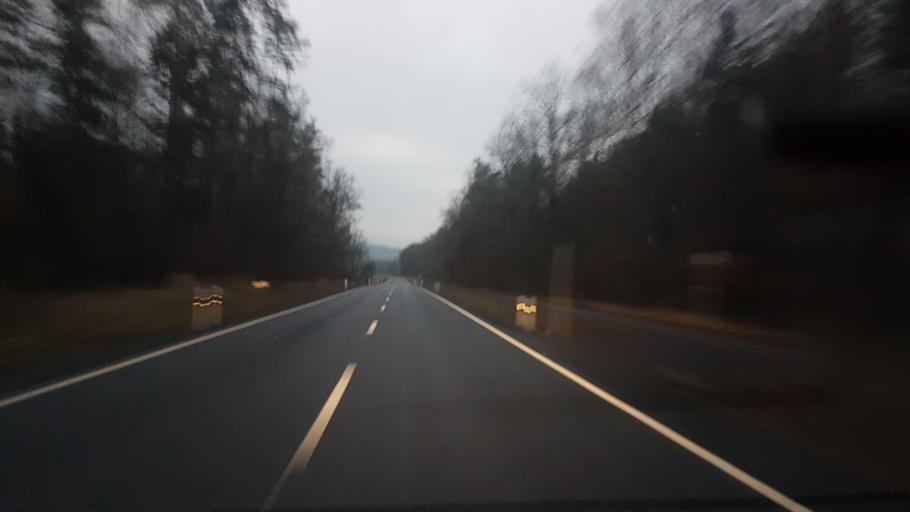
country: DE
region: Bavaria
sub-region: Regierungsbezirk Unterfranken
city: Ermershausen
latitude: 50.2250
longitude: 10.5923
